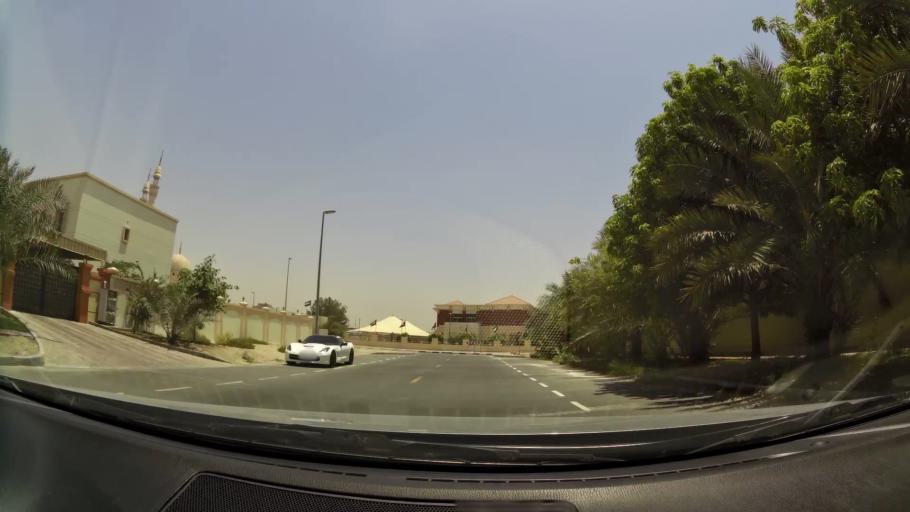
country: AE
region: Dubai
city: Dubai
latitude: 25.0940
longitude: 55.1984
